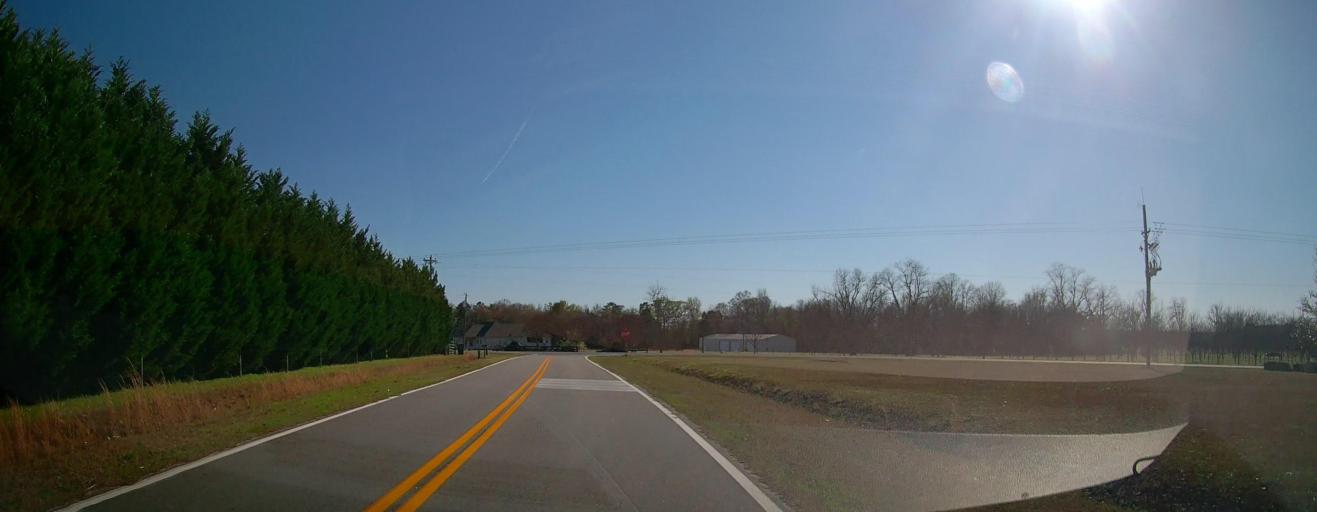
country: US
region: Georgia
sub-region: Peach County
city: Byron
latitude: 32.6740
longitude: -83.8347
